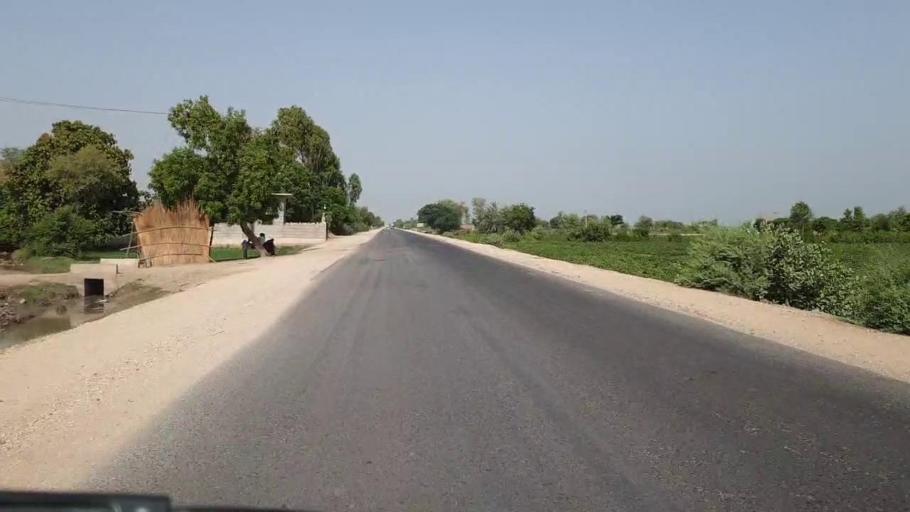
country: PK
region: Sindh
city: Sakrand
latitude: 26.2451
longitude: 68.2461
